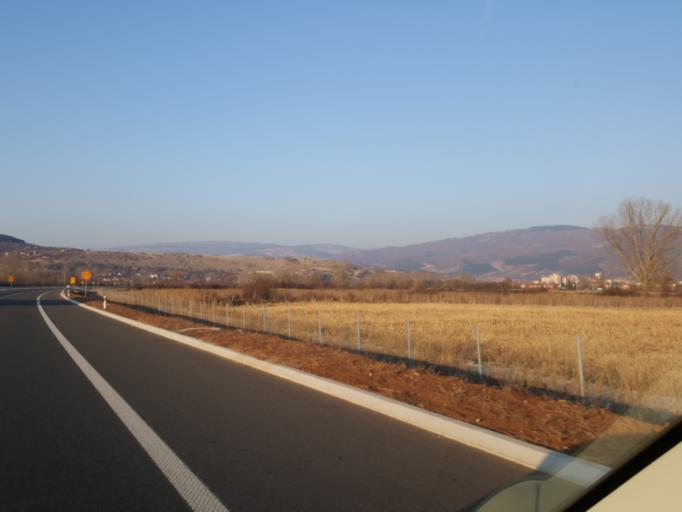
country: RS
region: Central Serbia
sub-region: Pirotski Okrug
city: Pirot
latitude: 43.1439
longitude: 22.5676
